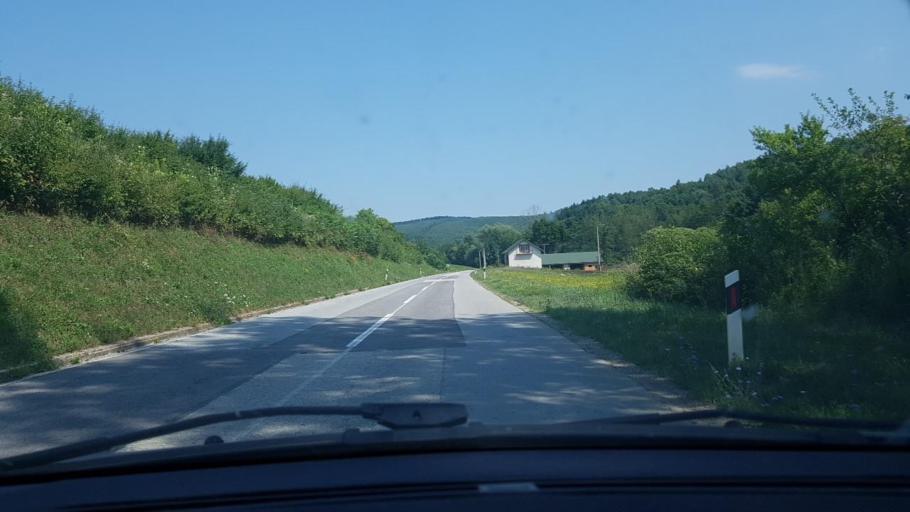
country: BA
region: Federation of Bosnia and Herzegovina
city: Velika Kladusa
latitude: 45.2329
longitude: 15.7350
